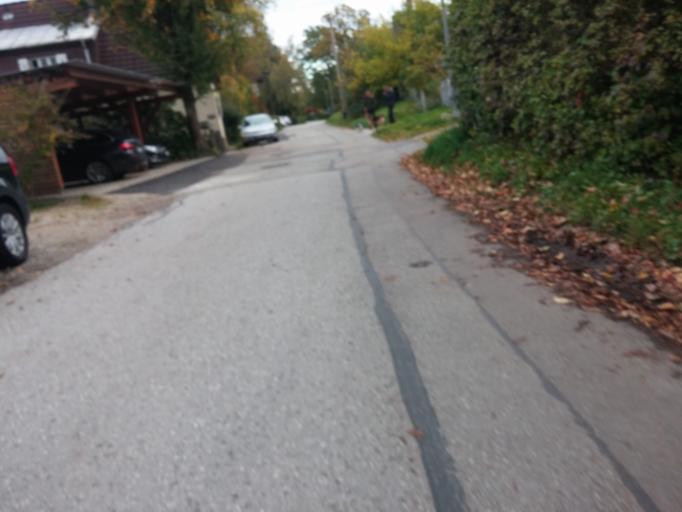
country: DE
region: Bavaria
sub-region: Upper Bavaria
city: Kirchseeon
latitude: 48.0761
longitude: 11.8797
